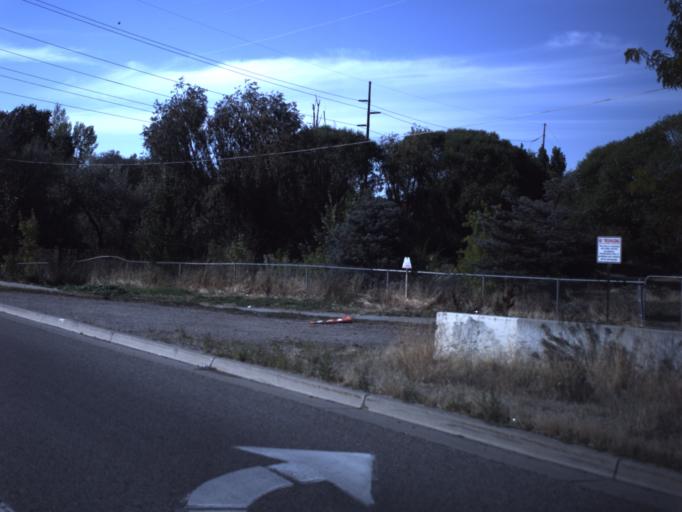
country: US
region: Utah
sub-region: Salt Lake County
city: Murray
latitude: 40.6656
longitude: -111.8640
